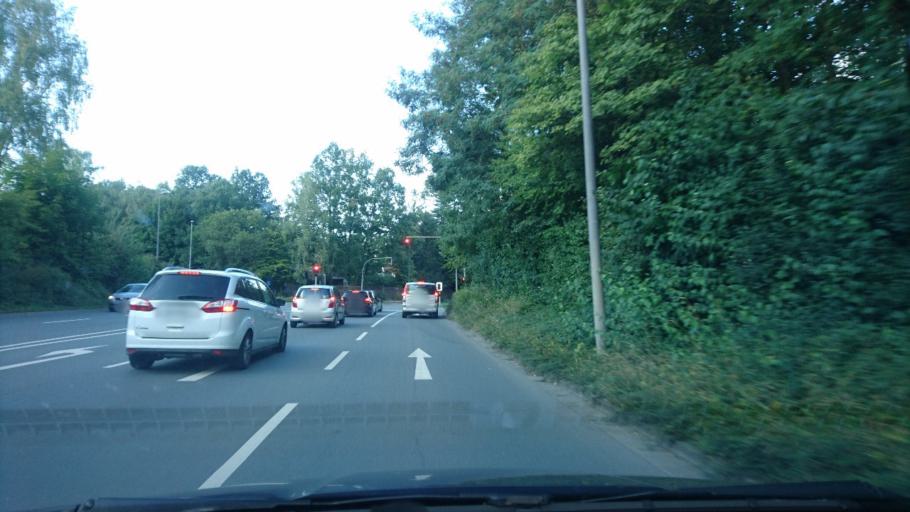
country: DE
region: Bavaria
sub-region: Upper Franconia
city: Bayreuth
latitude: 49.9488
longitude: 11.5562
